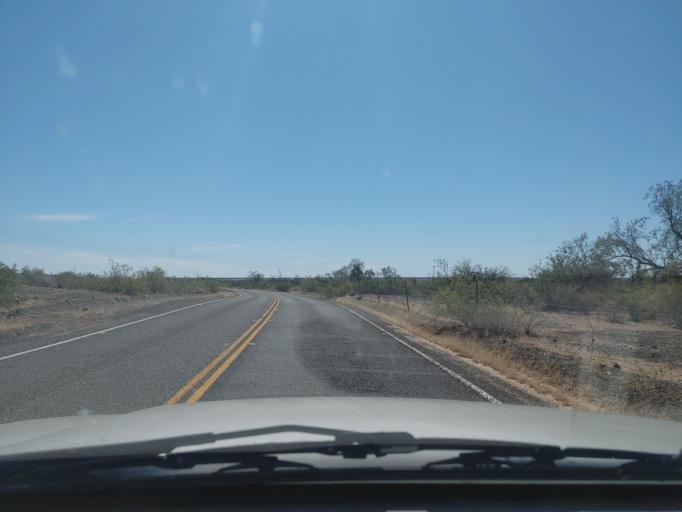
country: US
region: Arizona
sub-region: Maricopa County
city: Gila Bend
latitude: 32.9862
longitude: -113.3299
